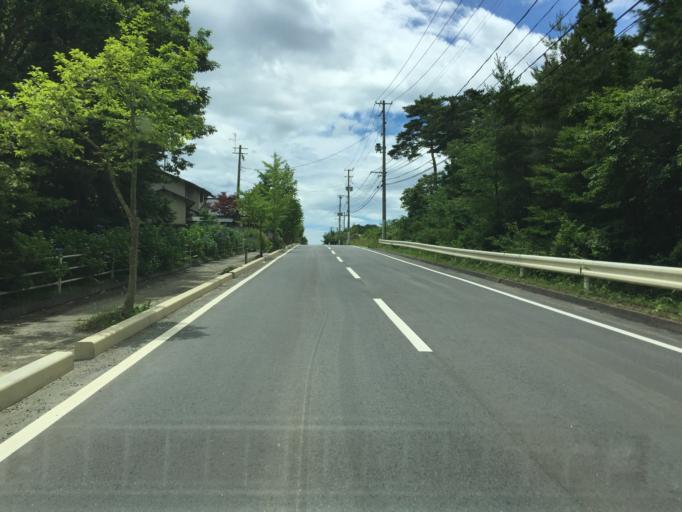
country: JP
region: Fukushima
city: Namie
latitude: 37.6580
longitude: 141.0087
